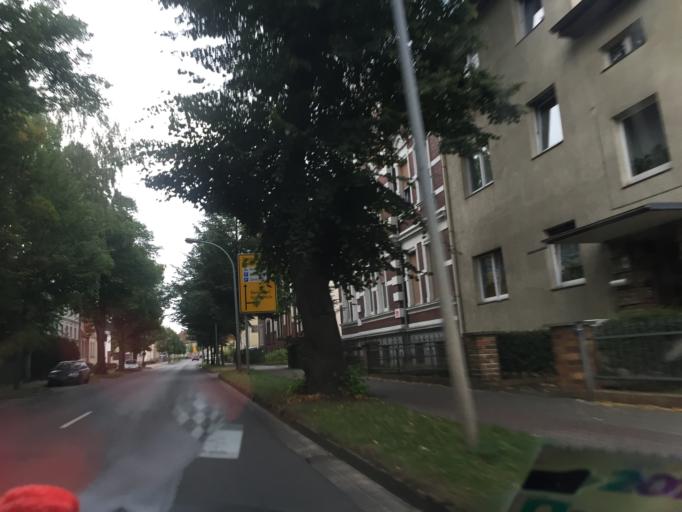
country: DE
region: Brandenburg
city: Zehdenick
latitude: 52.9786
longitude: 13.3255
